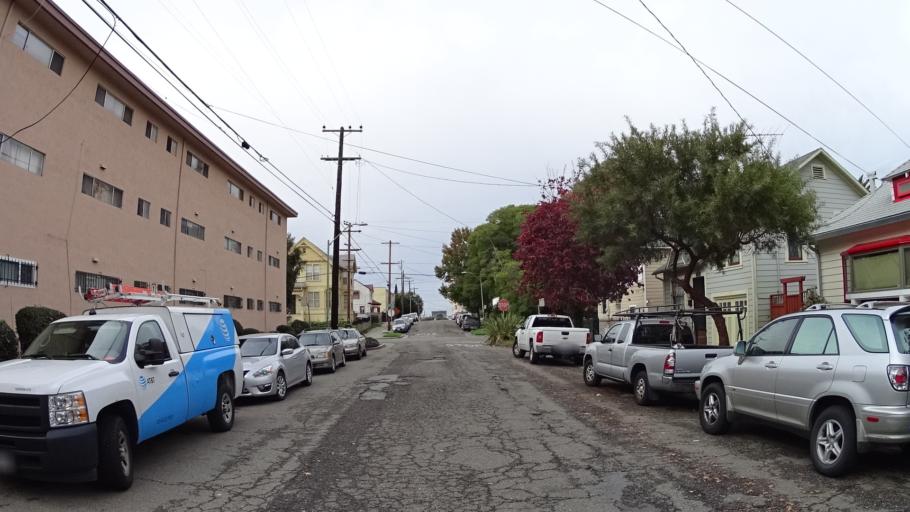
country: US
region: California
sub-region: Alameda County
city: Oakland
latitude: 37.7965
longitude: -122.2464
